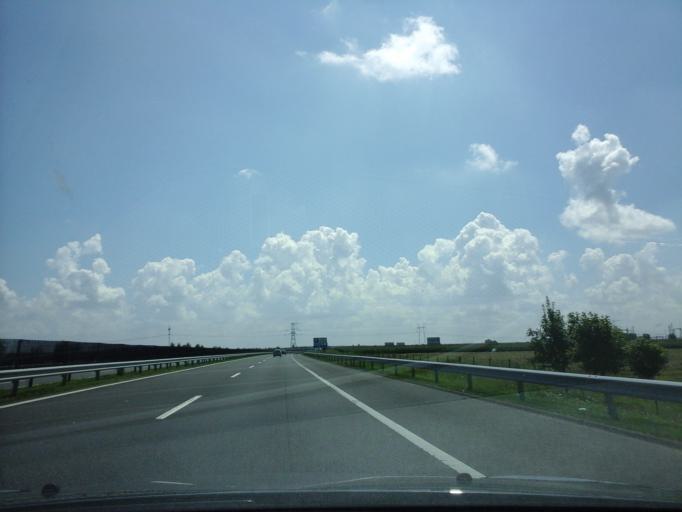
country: HU
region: Hajdu-Bihar
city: Hajduboszormeny
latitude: 47.6257
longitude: 21.5132
